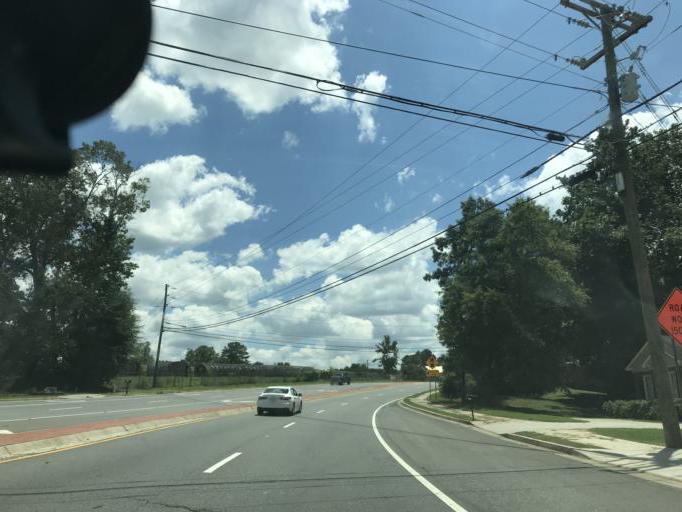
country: US
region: Georgia
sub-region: Fulton County
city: Milton
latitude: 34.1345
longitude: -84.2274
